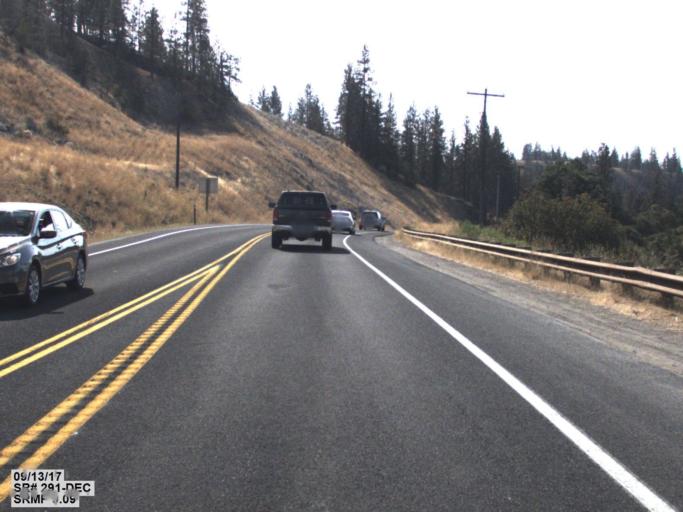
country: US
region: Washington
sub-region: Spokane County
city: Fairwood
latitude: 47.7755
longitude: -117.5433
